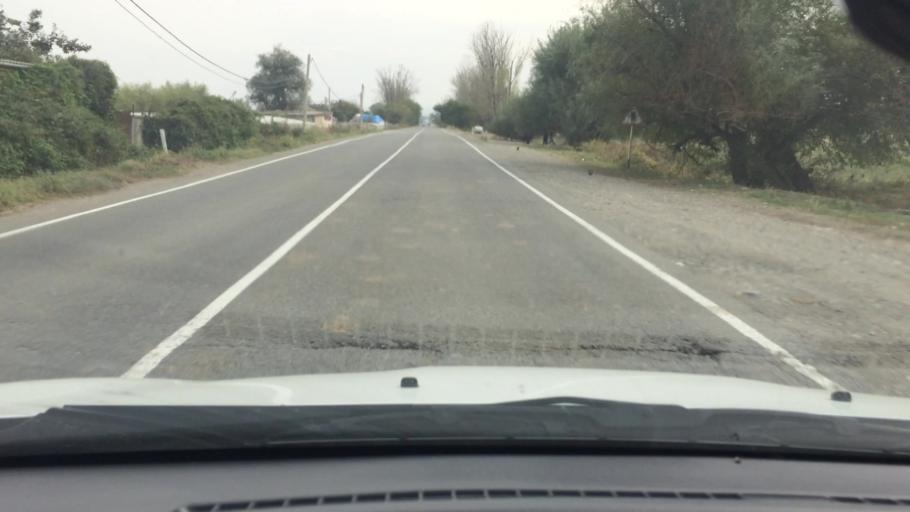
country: GE
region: Kvemo Kartli
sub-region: Gardabani
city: Gardabani
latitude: 41.4483
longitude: 44.9952
